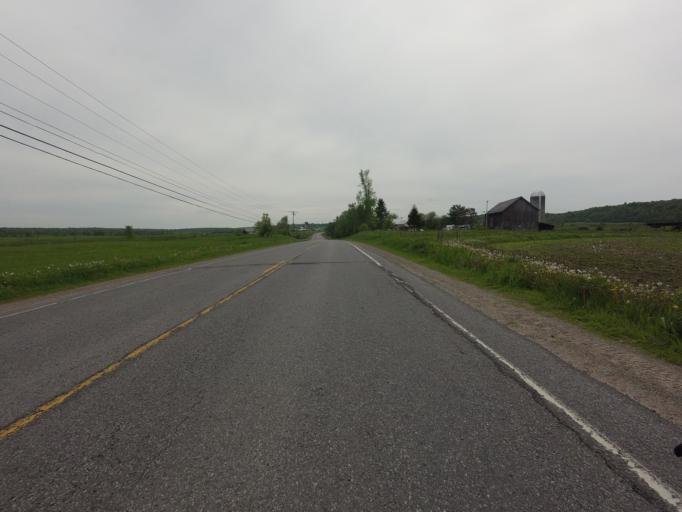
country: US
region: New York
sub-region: St. Lawrence County
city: Canton
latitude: 44.3533
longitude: -75.2150
